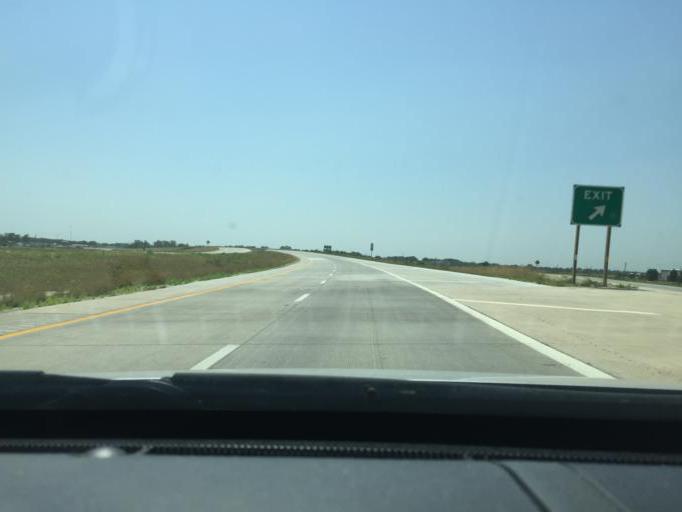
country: US
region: Kansas
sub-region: Reno County
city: South Hutchinson
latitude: 38.0290
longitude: -97.8983
